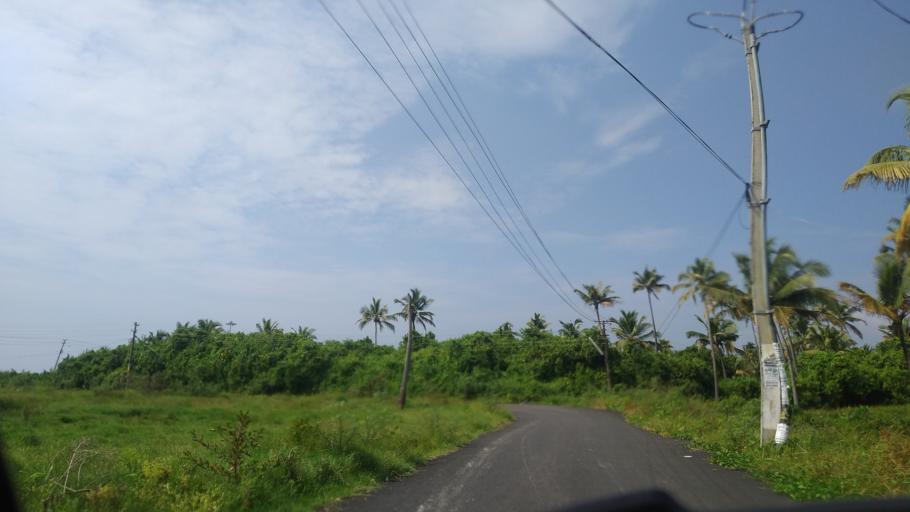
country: IN
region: Kerala
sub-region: Ernakulam
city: Elur
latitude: 10.0472
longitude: 76.2067
